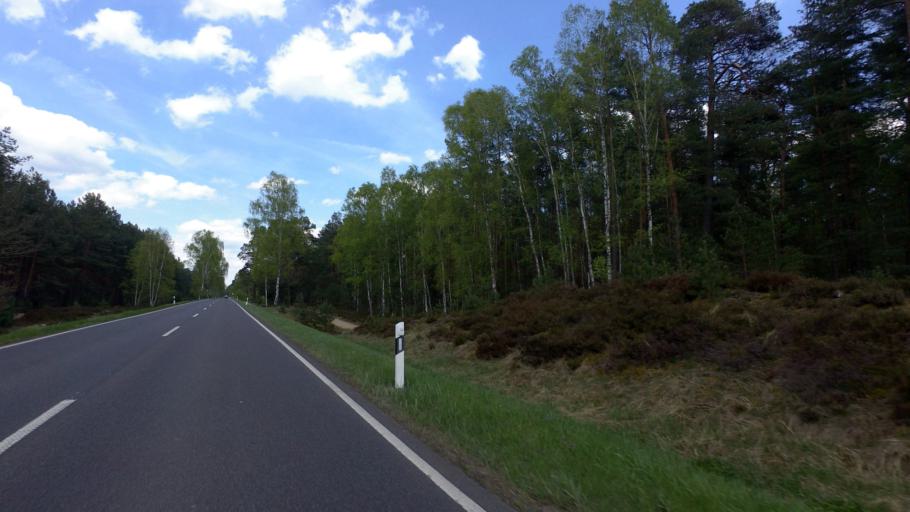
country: DE
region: Brandenburg
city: Marienwerder
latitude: 52.9663
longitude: 13.5732
